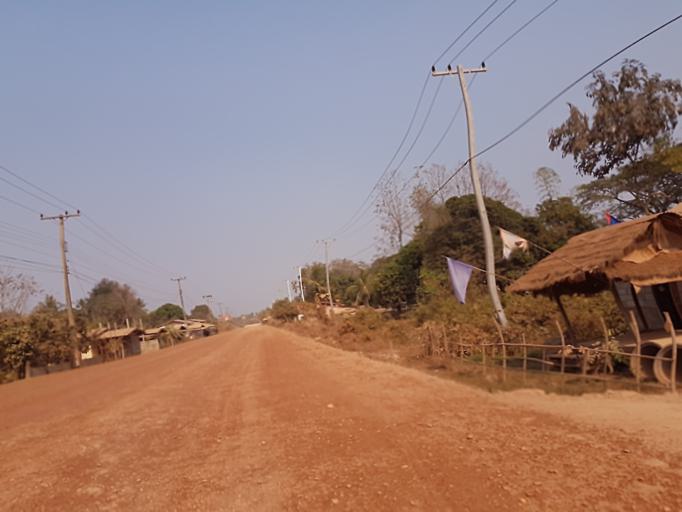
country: TH
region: Nong Khai
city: Nong Khai
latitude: 17.9392
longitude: 102.7901
